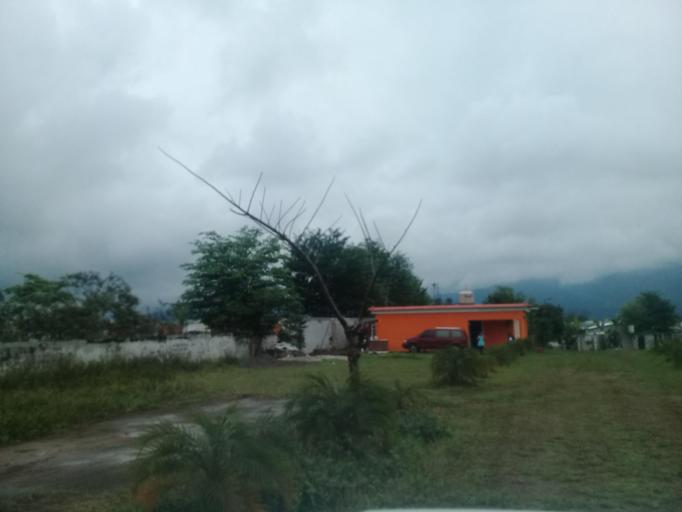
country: MX
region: Veracruz
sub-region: Cordoba
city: San Jose de Tapia
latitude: 18.8410
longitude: -96.9545
